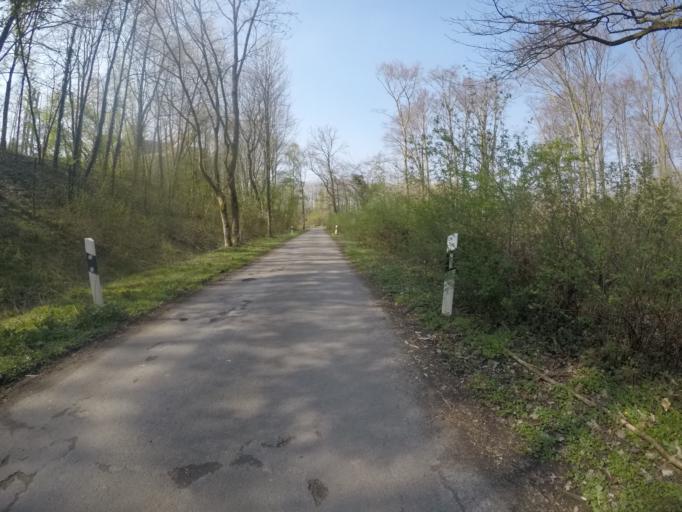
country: DE
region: North Rhine-Westphalia
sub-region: Regierungsbezirk Detmold
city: Bielefeld
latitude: 52.0433
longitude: 8.6089
